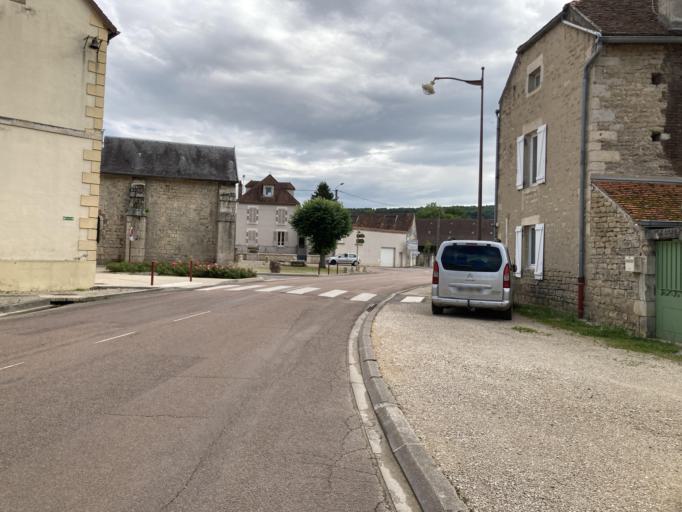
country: FR
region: Bourgogne
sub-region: Departement de la Cote-d'Or
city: Montbard
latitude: 47.6218
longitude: 4.3674
